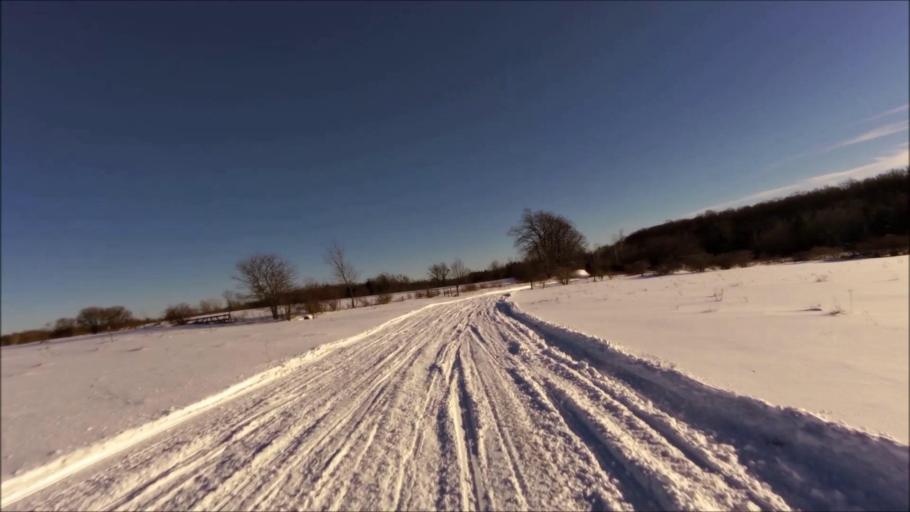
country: US
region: New York
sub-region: Chautauqua County
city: Mayville
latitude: 42.2587
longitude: -79.3869
